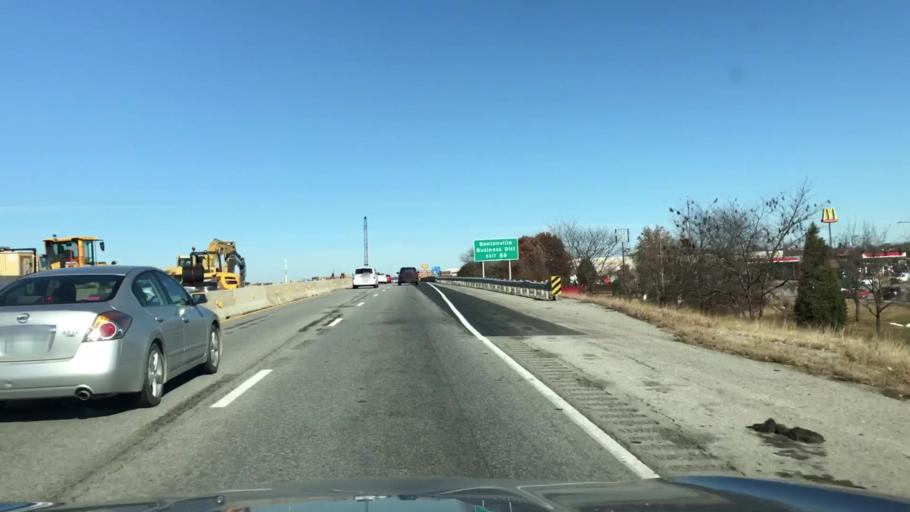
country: US
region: Arkansas
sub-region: Benton County
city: Bentonville
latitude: 36.3339
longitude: -94.1836
